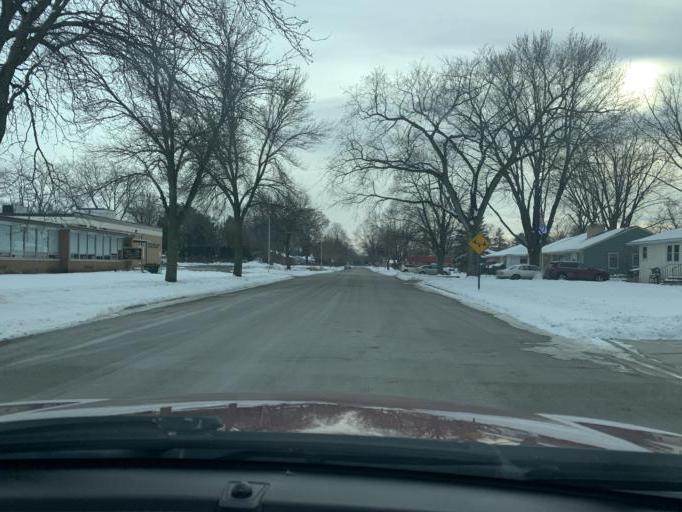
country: US
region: Minnesota
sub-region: Washington County
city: Saint Paul Park
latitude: 44.8417
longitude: -92.9886
